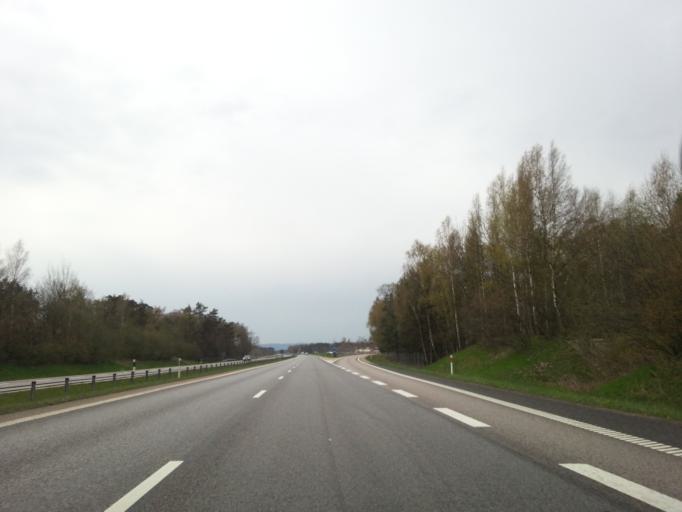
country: SE
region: Halland
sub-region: Laholms Kommun
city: Mellbystrand
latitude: 56.5100
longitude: 12.9622
